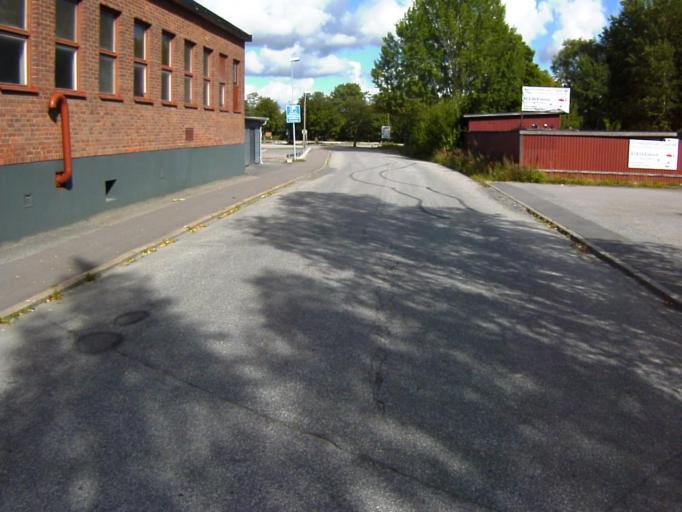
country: SE
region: Soedermanland
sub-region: Eskilstuna Kommun
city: Eskilstuna
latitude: 59.3785
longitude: 16.5001
